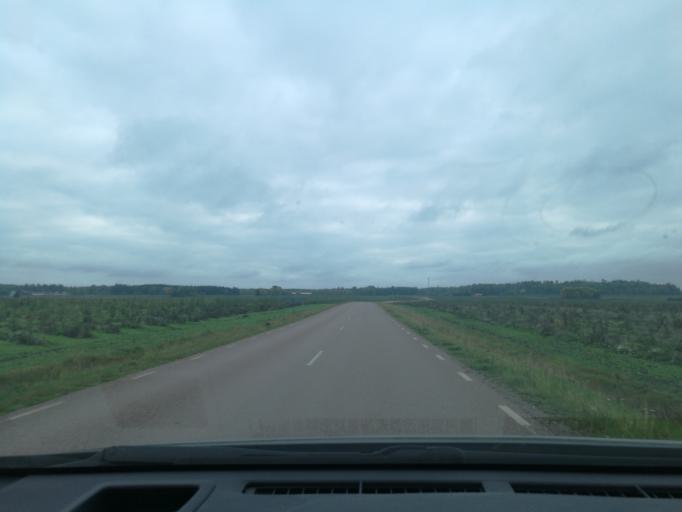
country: SE
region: Vaestmanland
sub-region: Vasteras
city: Tillberga
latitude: 59.7089
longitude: 16.6595
